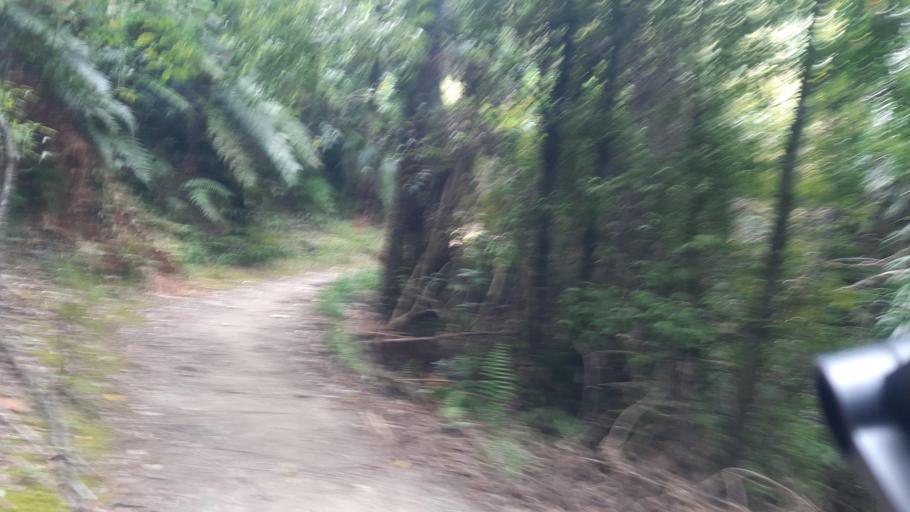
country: NZ
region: Marlborough
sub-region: Marlborough District
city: Picton
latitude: -41.2460
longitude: 173.9565
